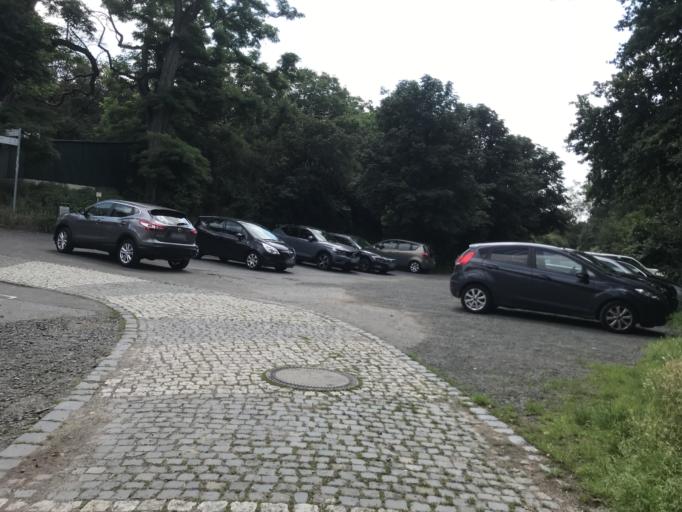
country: DE
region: Hesse
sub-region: Regierungsbezirk Darmstadt
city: Bischofsheim
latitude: 50.0110
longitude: 8.3912
